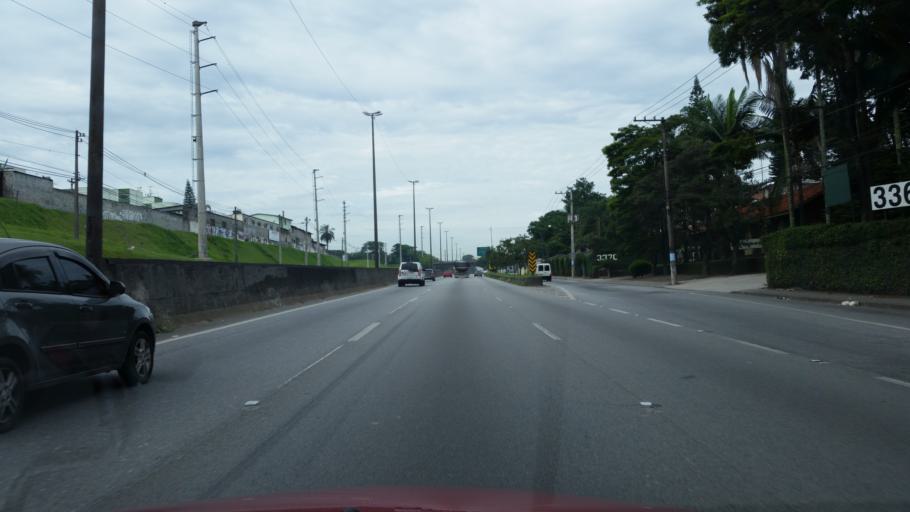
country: BR
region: Sao Paulo
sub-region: Taboao Da Serra
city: Taboao da Serra
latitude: -23.6142
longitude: -46.7837
